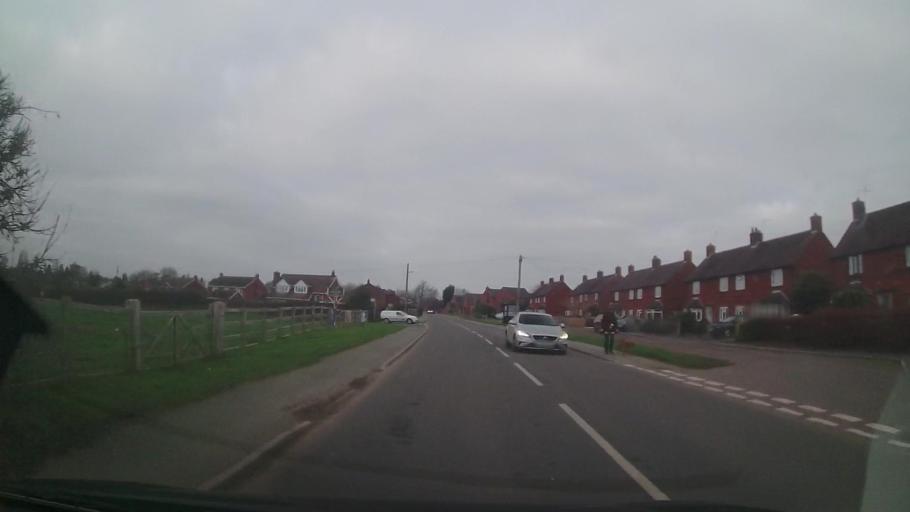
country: GB
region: England
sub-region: Shropshire
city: Great Ness
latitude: 52.7887
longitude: -2.8528
